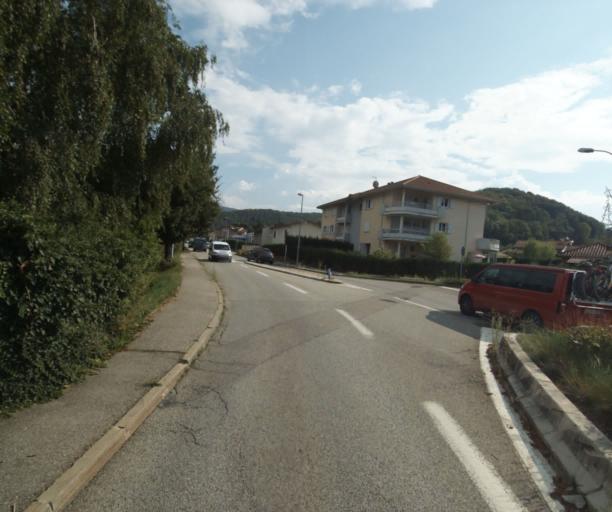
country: FR
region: Rhone-Alpes
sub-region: Departement de l'Isere
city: Brie-et-Angonnes
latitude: 45.1169
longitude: 5.7833
